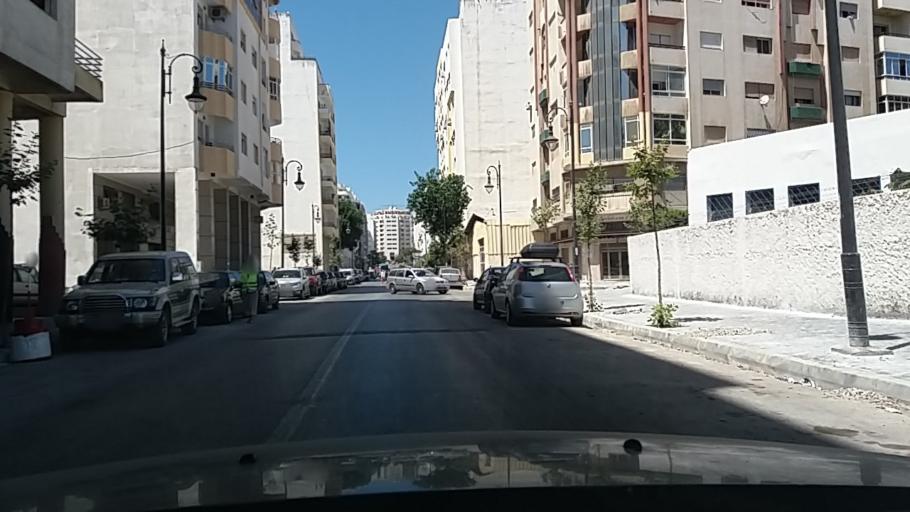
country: MA
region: Tanger-Tetouan
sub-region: Tanger-Assilah
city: Tangier
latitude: 35.7720
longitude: -5.7995
